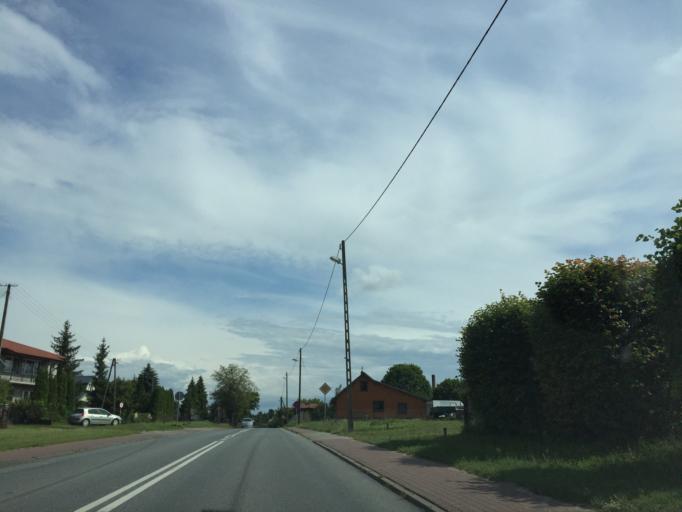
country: PL
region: Masovian Voivodeship
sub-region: Powiat losicki
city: Sarnaki
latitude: 52.3189
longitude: 22.8847
